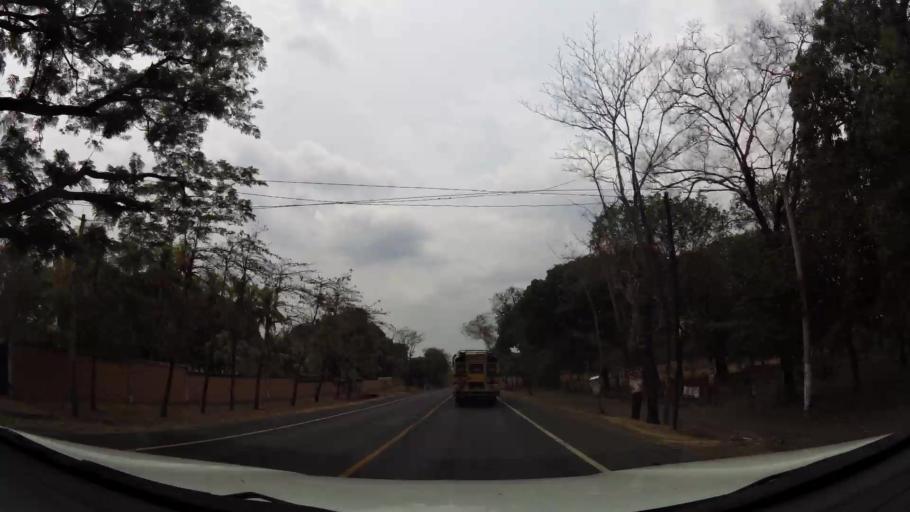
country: NI
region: Leon
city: Telica
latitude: 12.5140
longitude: -86.8624
